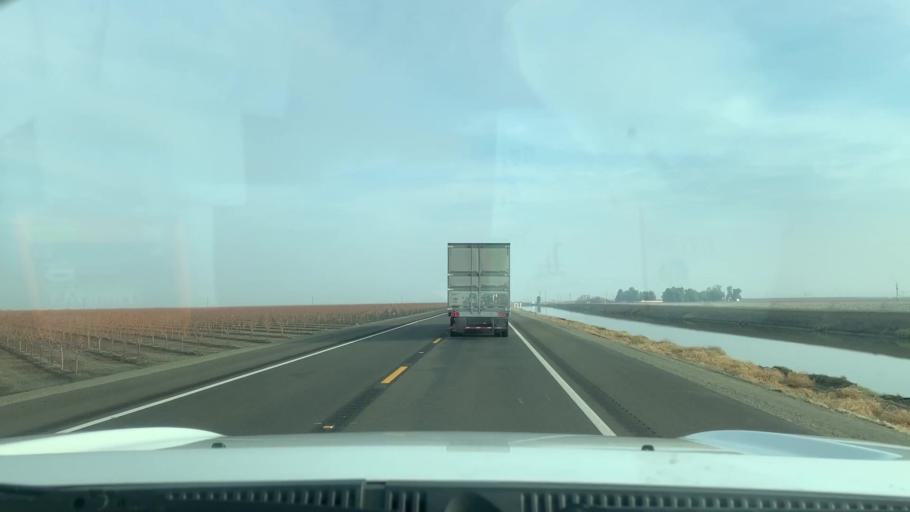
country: US
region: California
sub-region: Kings County
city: Stratford
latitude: 36.1318
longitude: -119.8843
